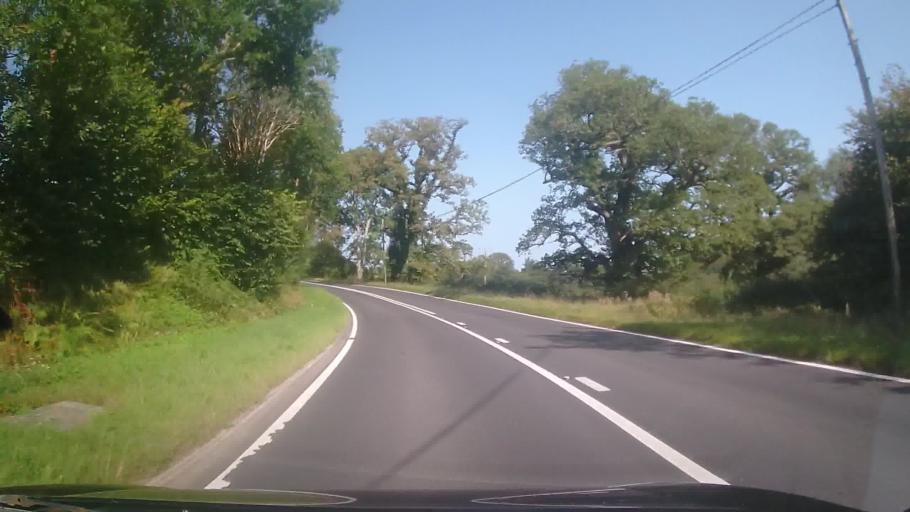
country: GB
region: Wales
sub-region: Sir Powys
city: Builth Wells
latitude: 52.1370
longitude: -3.5502
